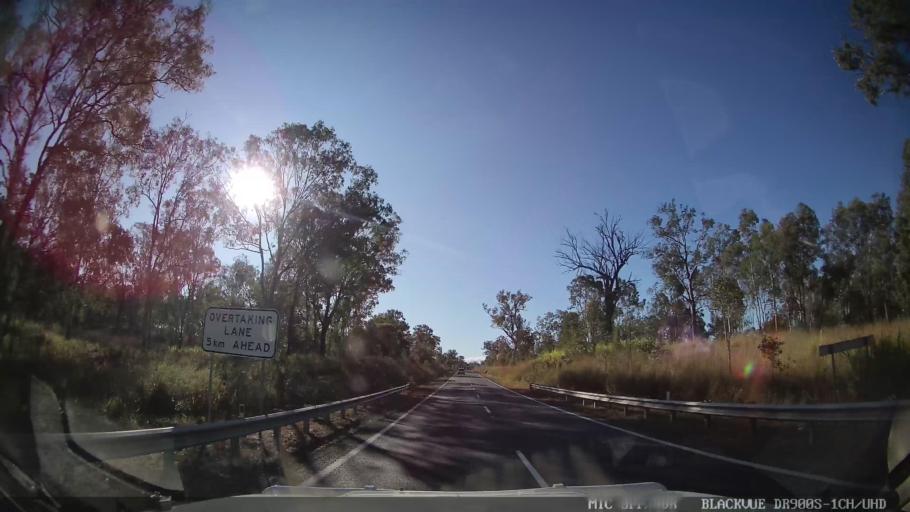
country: AU
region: Queensland
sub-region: Bundaberg
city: Sharon
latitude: -24.8277
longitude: 151.7077
